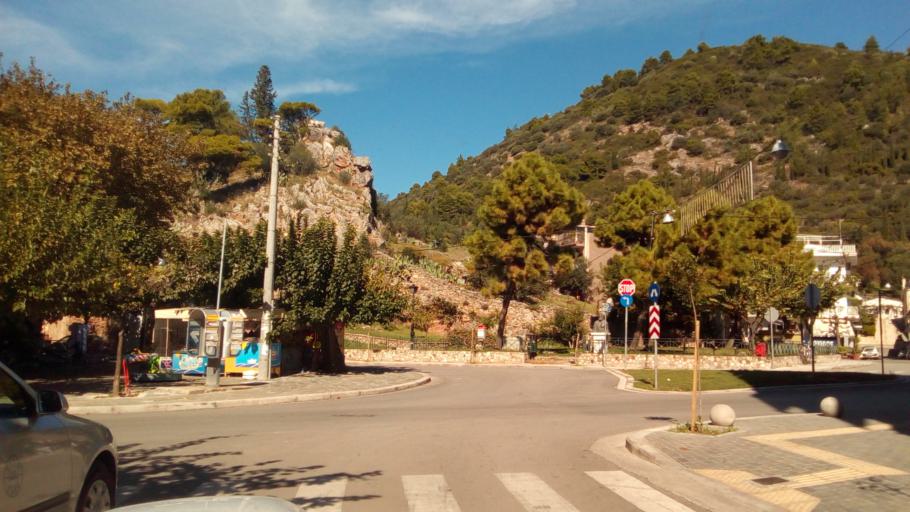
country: GR
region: West Greece
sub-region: Nomos Aitolias kai Akarnanias
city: Nafpaktos
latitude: 38.3940
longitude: 21.8392
